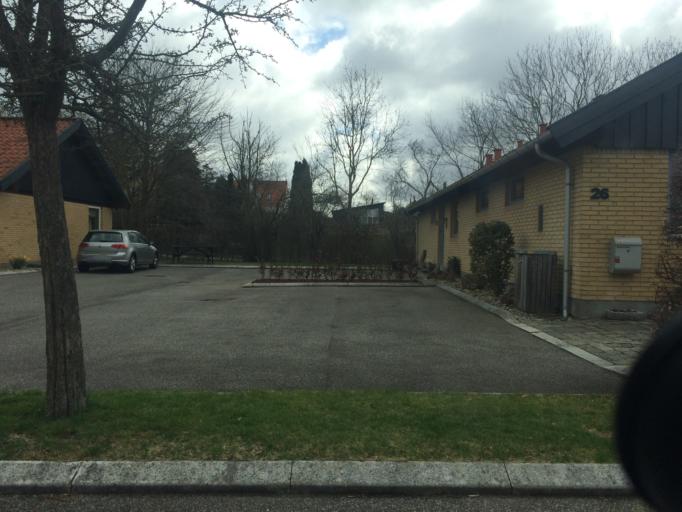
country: DK
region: Capital Region
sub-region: Ballerup Kommune
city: Ballerup
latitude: 55.7525
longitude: 12.3772
